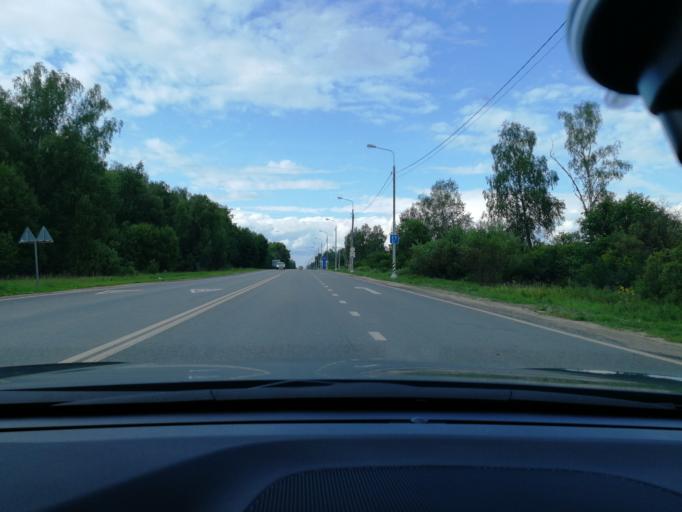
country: RU
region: Moskovskaya
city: Proletarskiy
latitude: 55.0422
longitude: 37.4308
